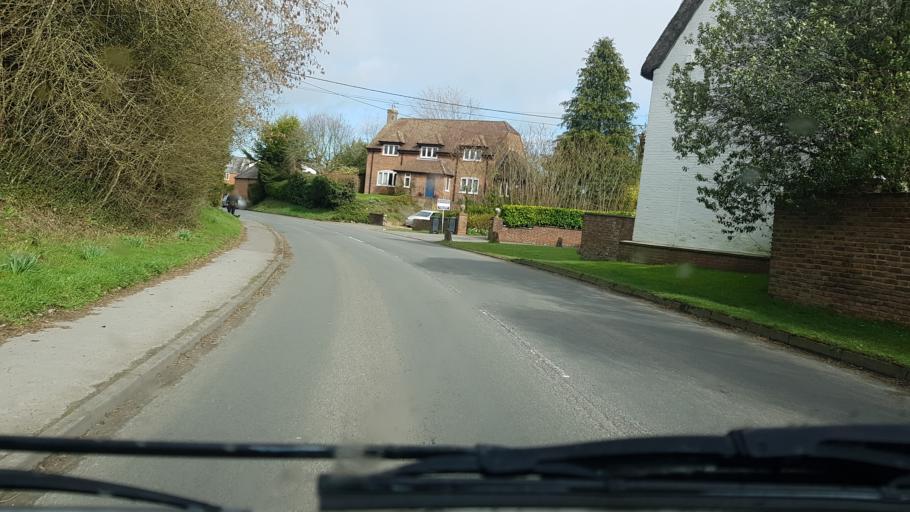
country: GB
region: England
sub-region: Wiltshire
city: Market Lavington
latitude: 51.3111
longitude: -1.9441
